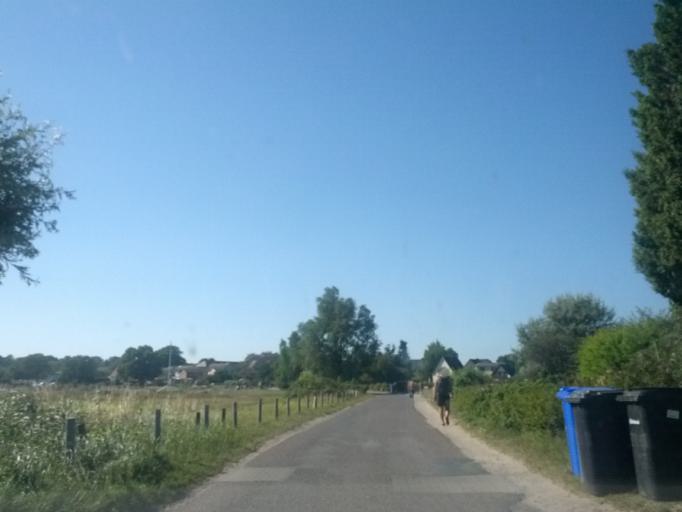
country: DE
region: Mecklenburg-Vorpommern
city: Ostseebad Sellin
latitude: 54.3298
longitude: 13.6782
